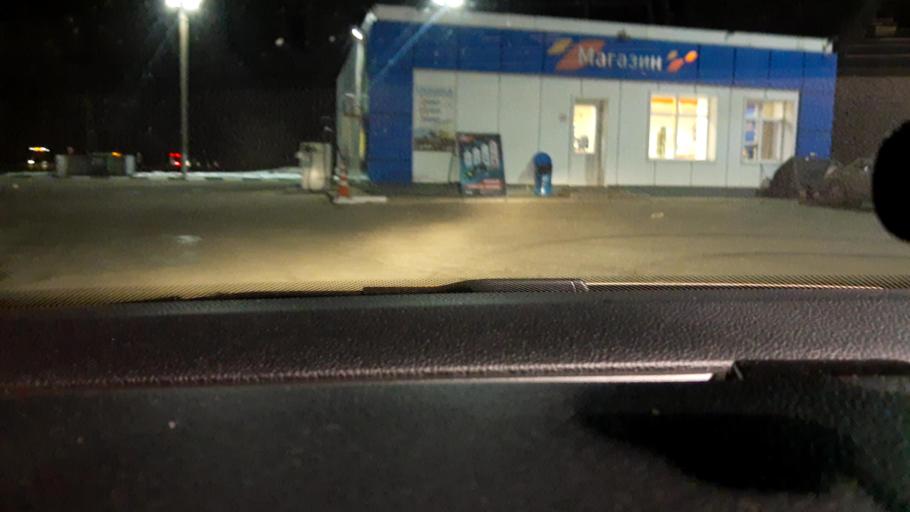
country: RU
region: Vladimir
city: Lakinsk
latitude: 55.9674
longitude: 39.7854
